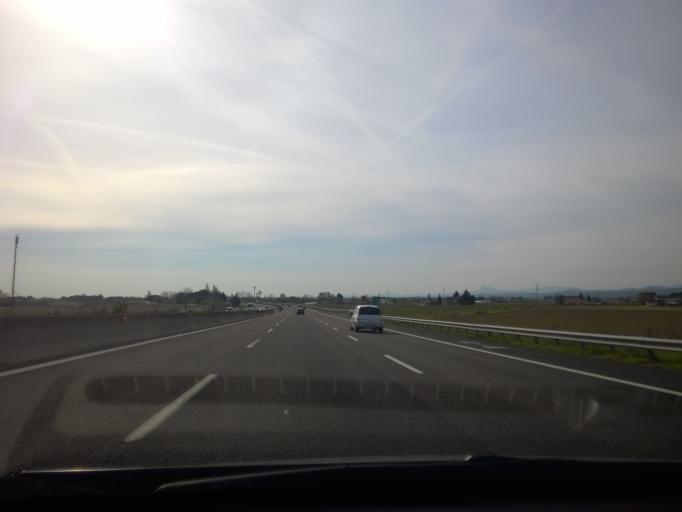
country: IT
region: Emilia-Romagna
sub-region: Forli-Cesena
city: Bagnarola
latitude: 44.1503
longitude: 12.3210
